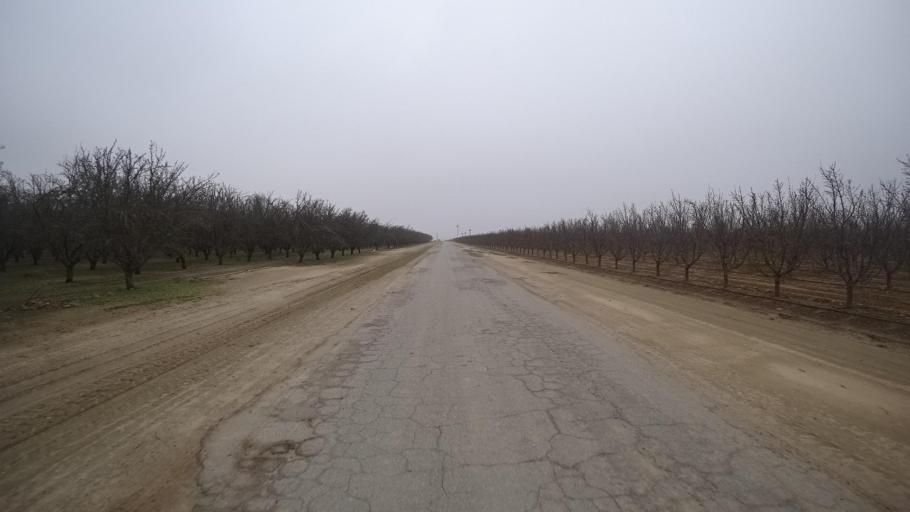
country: US
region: California
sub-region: Kern County
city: Lost Hills
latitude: 35.5831
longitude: -119.5360
